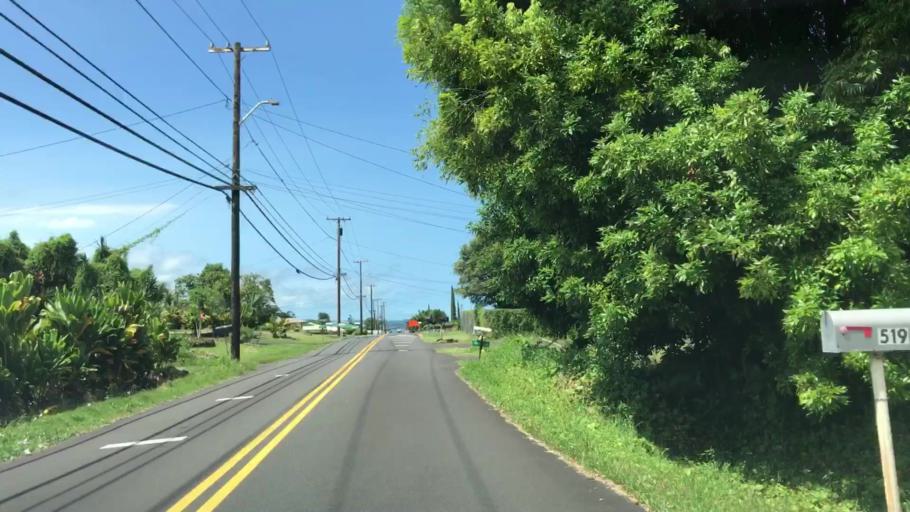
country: US
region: Hawaii
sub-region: Hawaii County
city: Hilo
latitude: 19.6801
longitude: -155.0802
